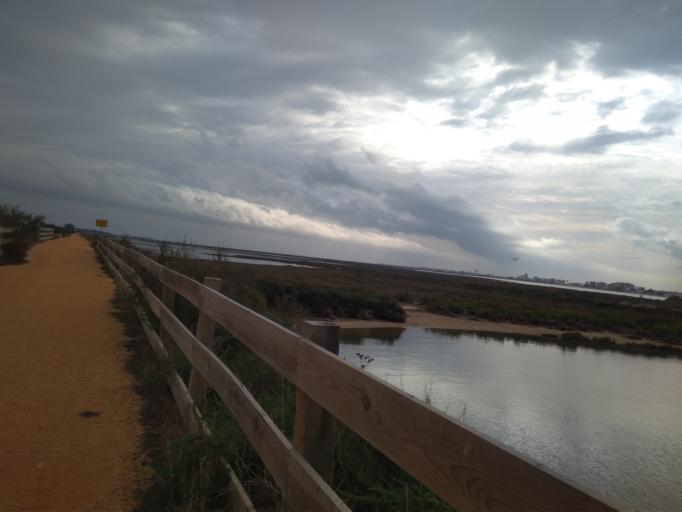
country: PT
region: Faro
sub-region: Faro
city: Faro
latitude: 37.0189
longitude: -8.0010
